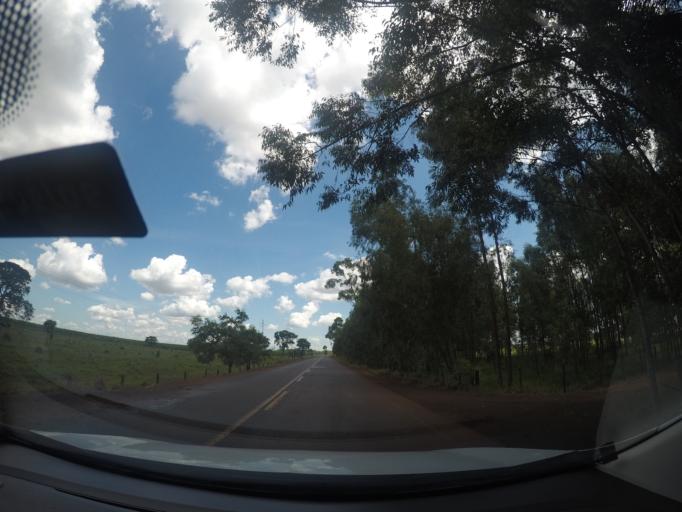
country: BR
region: Minas Gerais
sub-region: Frutal
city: Frutal
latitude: -19.8422
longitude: -48.7366
